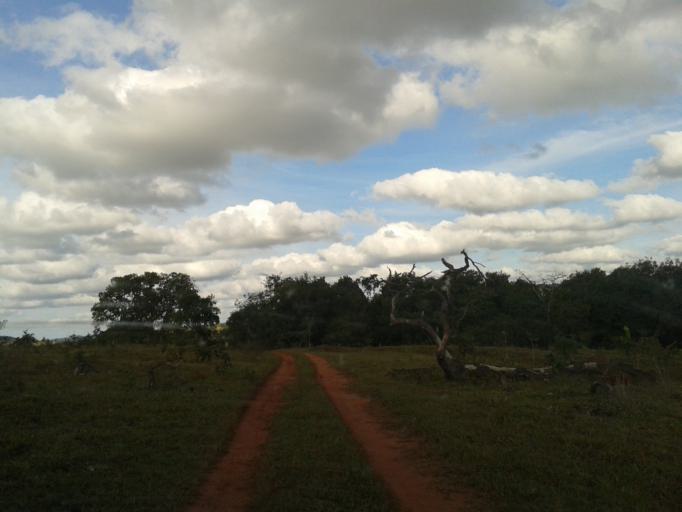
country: BR
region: Minas Gerais
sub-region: Campina Verde
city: Campina Verde
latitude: -19.4257
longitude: -49.7424
